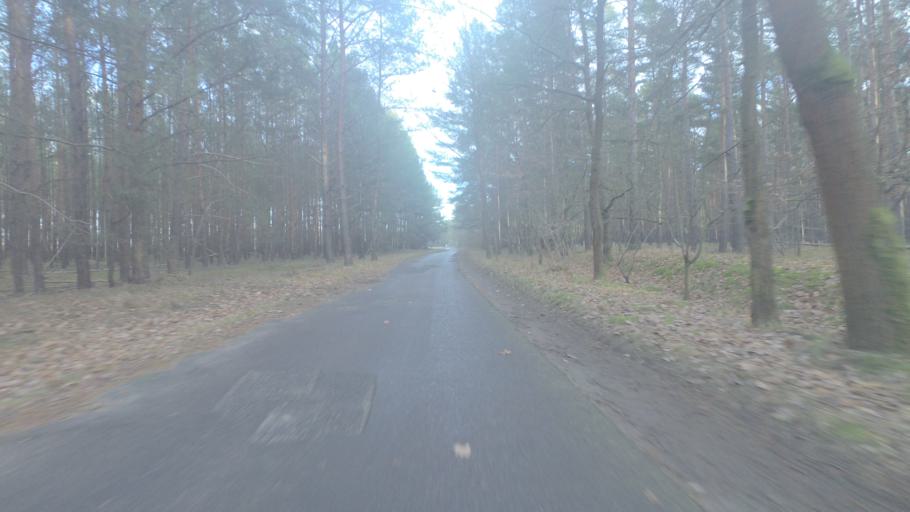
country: DE
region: Brandenburg
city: Zossen
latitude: 52.2187
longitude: 13.4947
